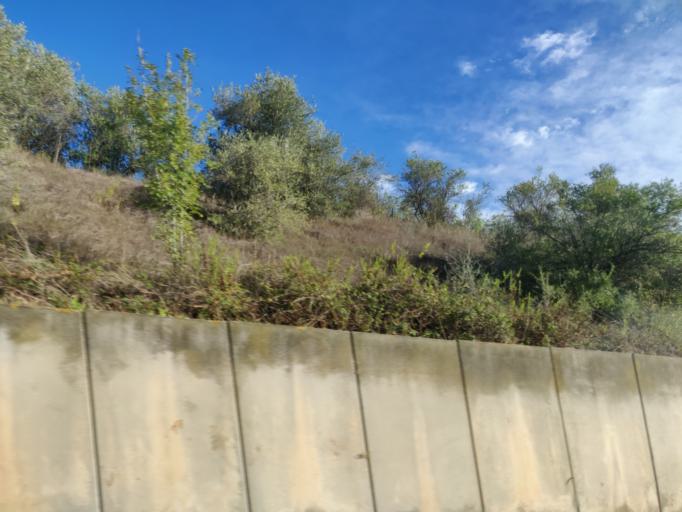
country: IT
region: Tuscany
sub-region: Provincia di Grosseto
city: Gavorrano
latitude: 42.9504
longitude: 10.8870
